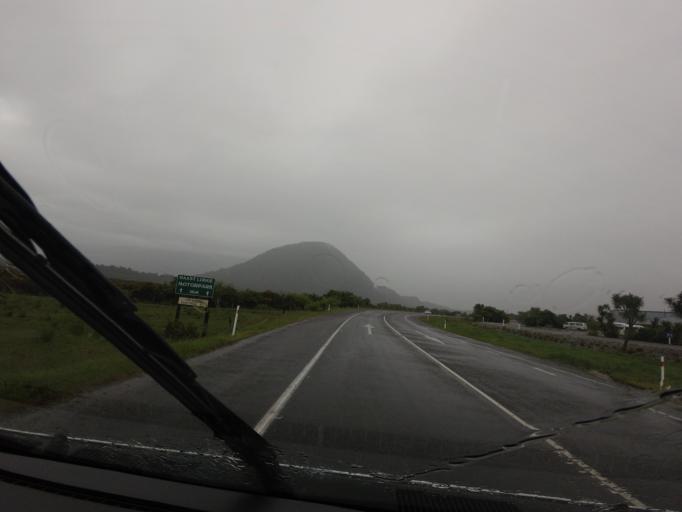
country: NZ
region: Otago
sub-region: Queenstown-Lakes District
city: Wanaka
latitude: -43.8566
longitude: 169.0476
